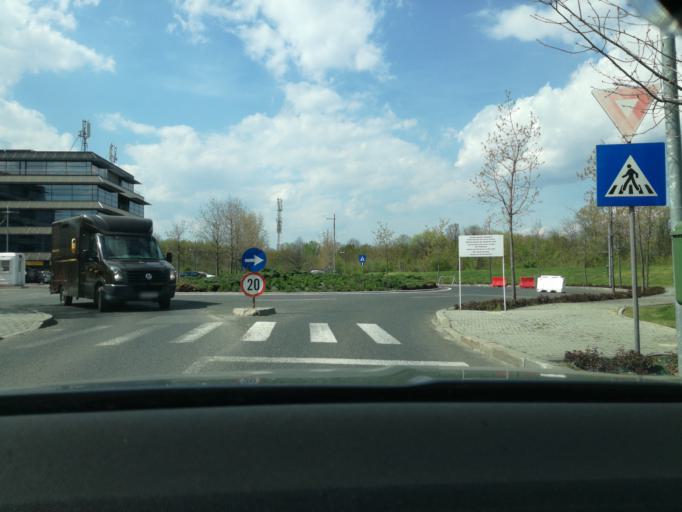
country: RO
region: Ilfov
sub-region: Comuna Otopeni
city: Otopeni
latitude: 44.5158
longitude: 26.0822
